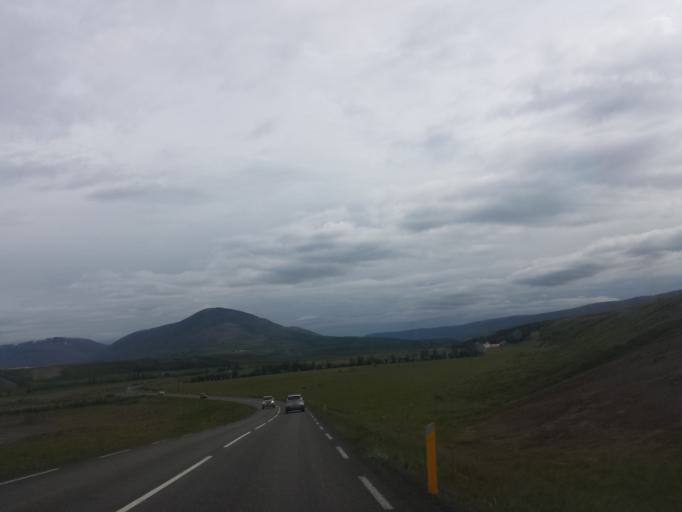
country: IS
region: Northeast
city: Akureyri
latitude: 65.7765
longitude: -17.9186
